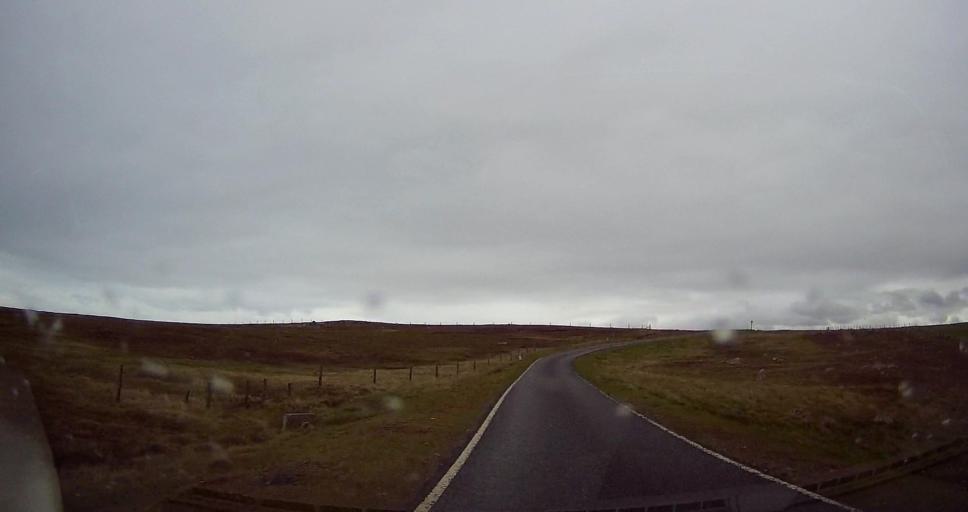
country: GB
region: Scotland
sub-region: Shetland Islands
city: Lerwick
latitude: 60.4859
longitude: -1.6059
